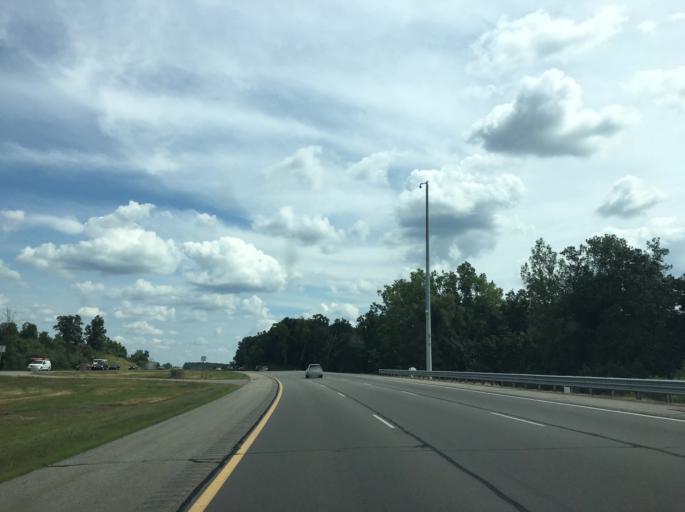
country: US
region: Michigan
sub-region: Oakland County
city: Holly
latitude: 42.8530
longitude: -83.5910
